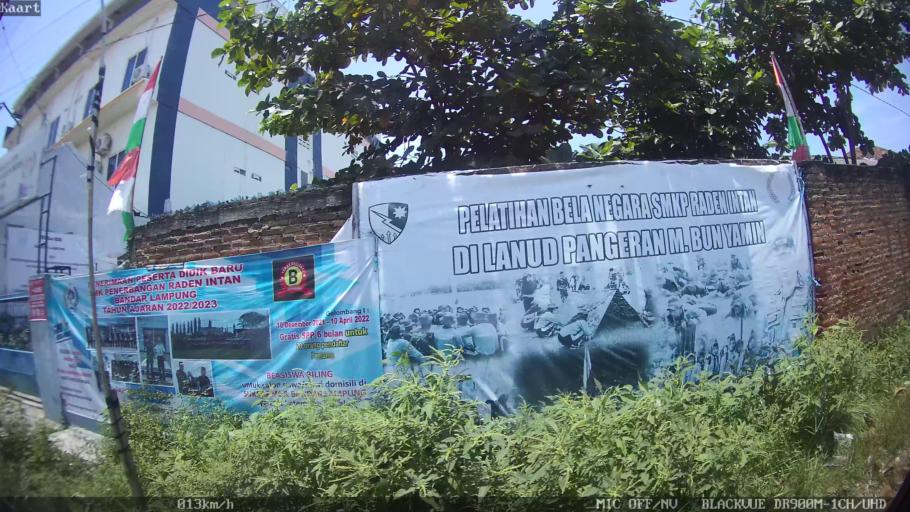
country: ID
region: Lampung
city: Kedaton
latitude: -5.3855
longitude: 105.2908
